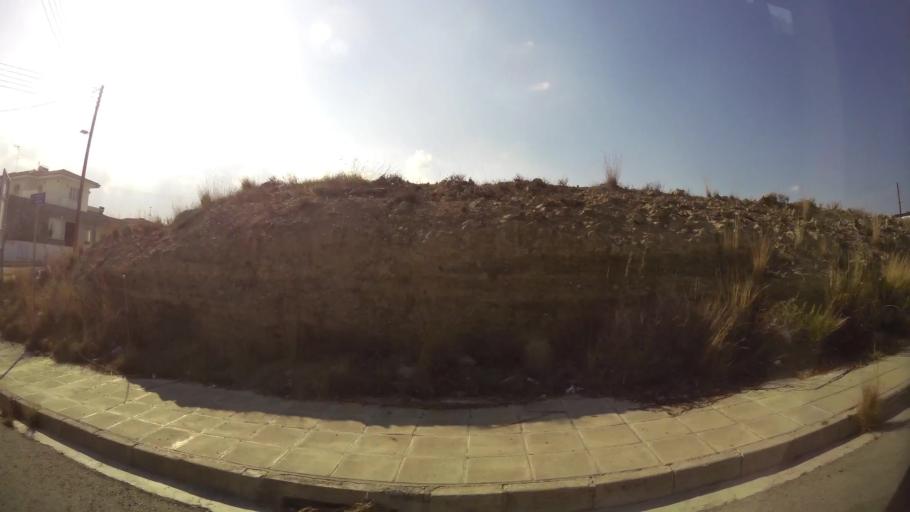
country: CY
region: Lefkosia
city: Kato Deftera
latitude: 35.1402
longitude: 33.2985
